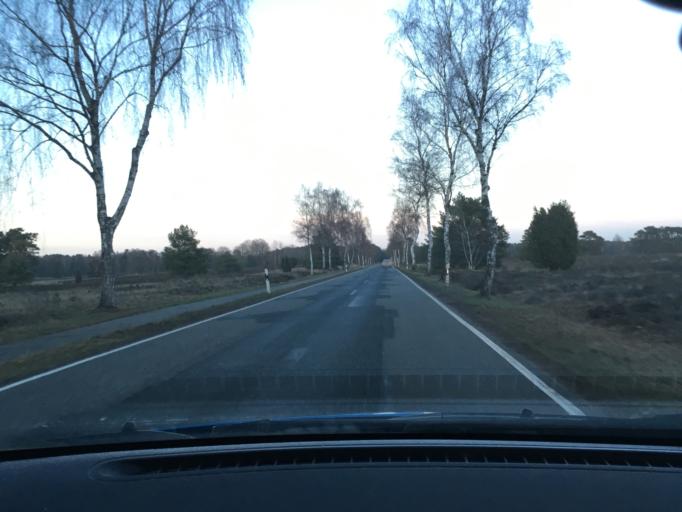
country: DE
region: Lower Saxony
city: Handeloh
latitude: 53.2410
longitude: 9.8674
